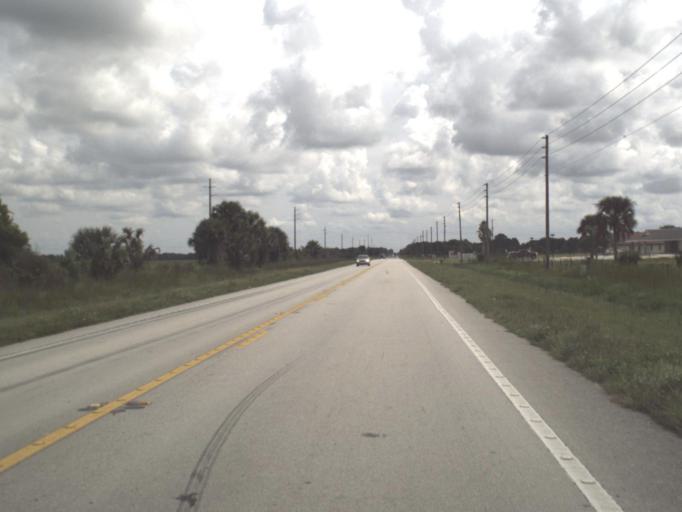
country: US
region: Florida
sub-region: Okeechobee County
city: Okeechobee
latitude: 27.2436
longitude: -80.9162
